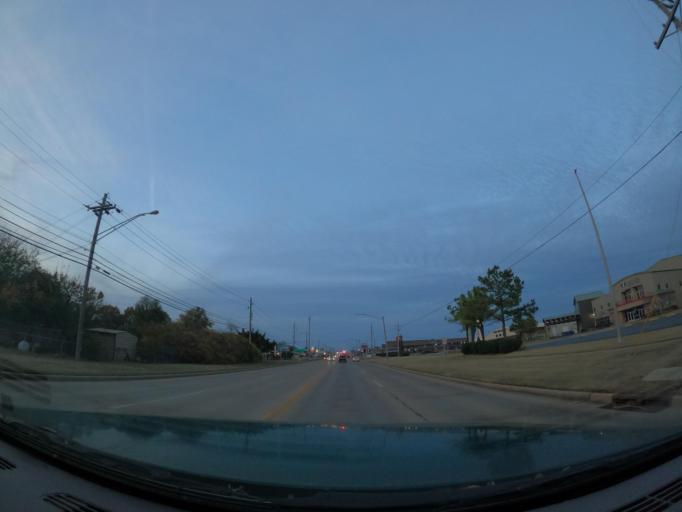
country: US
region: Oklahoma
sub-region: Tulsa County
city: Broken Arrow
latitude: 36.0655
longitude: -95.7974
